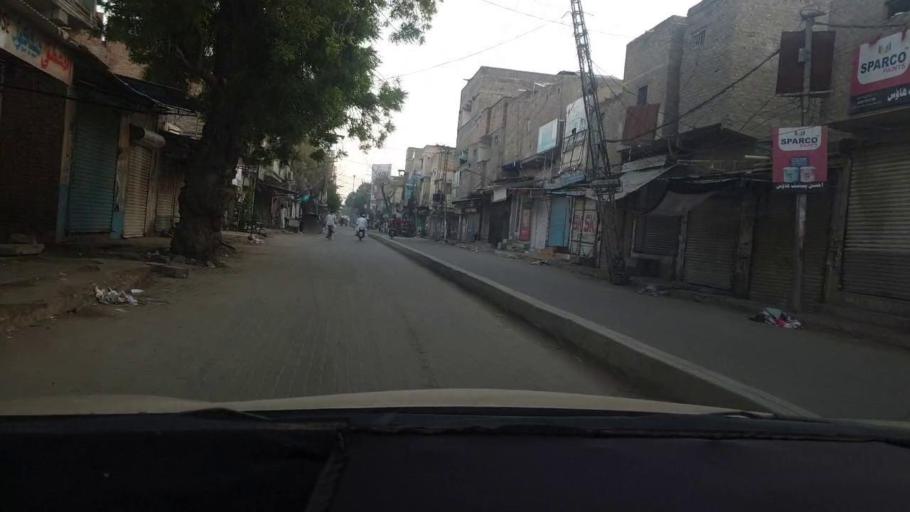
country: PK
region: Sindh
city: Larkana
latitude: 27.5513
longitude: 68.2149
